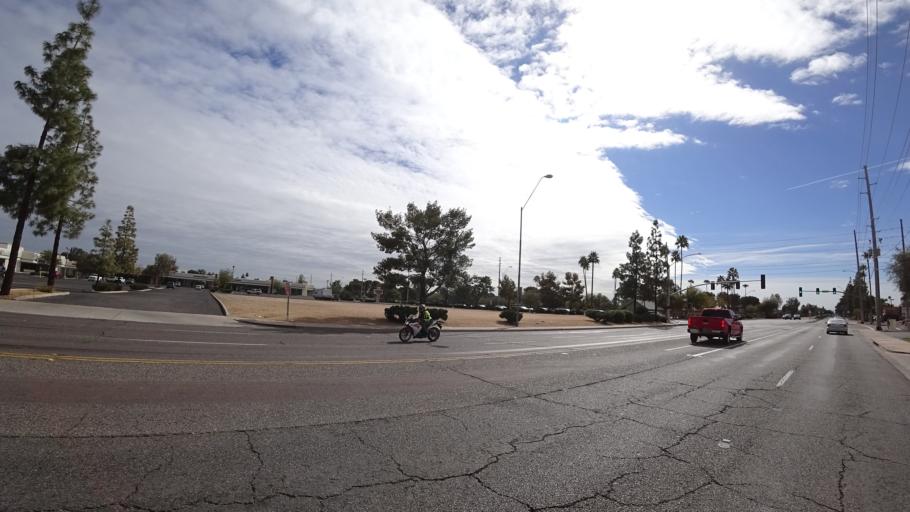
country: US
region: Arizona
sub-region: Maricopa County
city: Peoria
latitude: 33.6260
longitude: -112.1858
